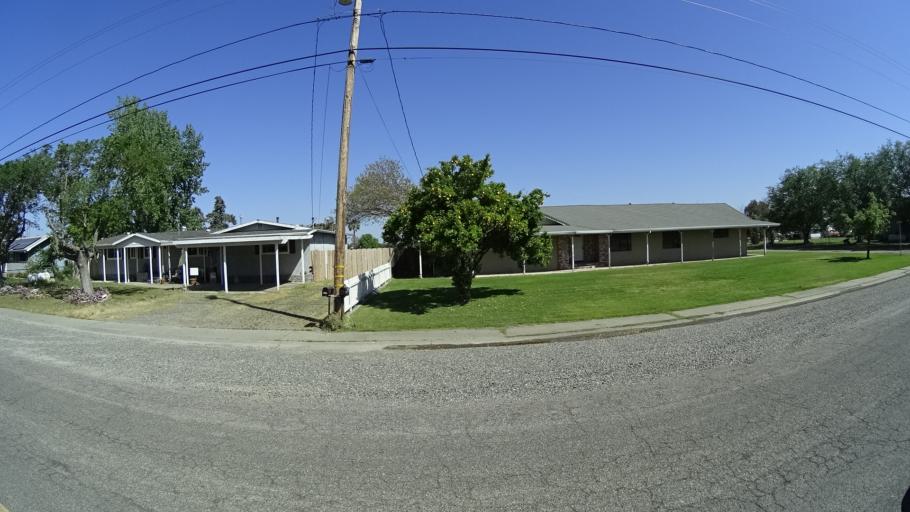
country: US
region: California
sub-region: Glenn County
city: Orland
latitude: 39.7254
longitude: -122.1748
